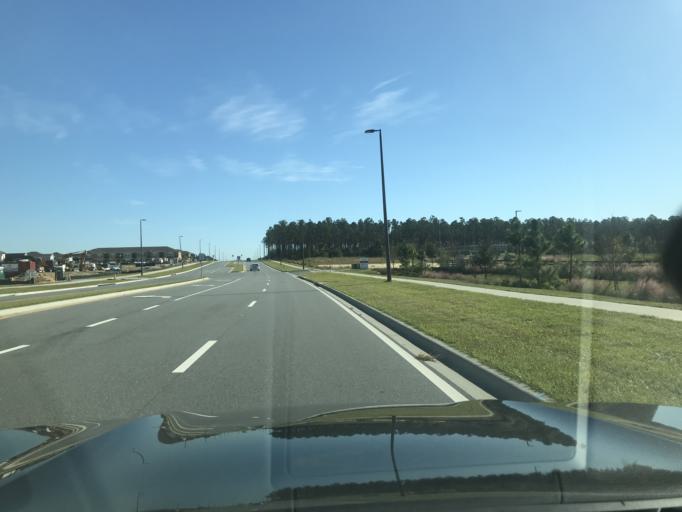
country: US
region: Florida
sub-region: Orange County
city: Oakland
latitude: 28.4597
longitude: -81.6336
